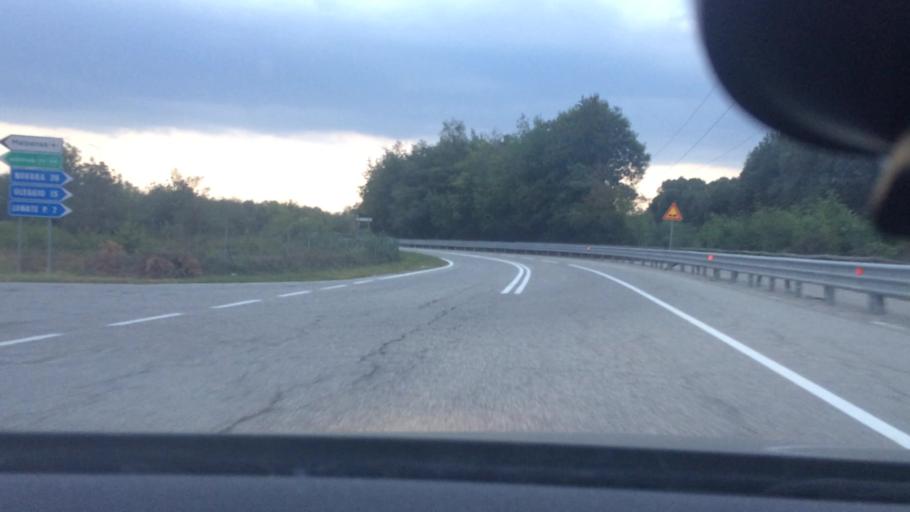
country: IT
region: Lombardy
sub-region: Provincia di Varese
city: Vizzola Ticino
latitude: 45.6109
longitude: 8.7087
